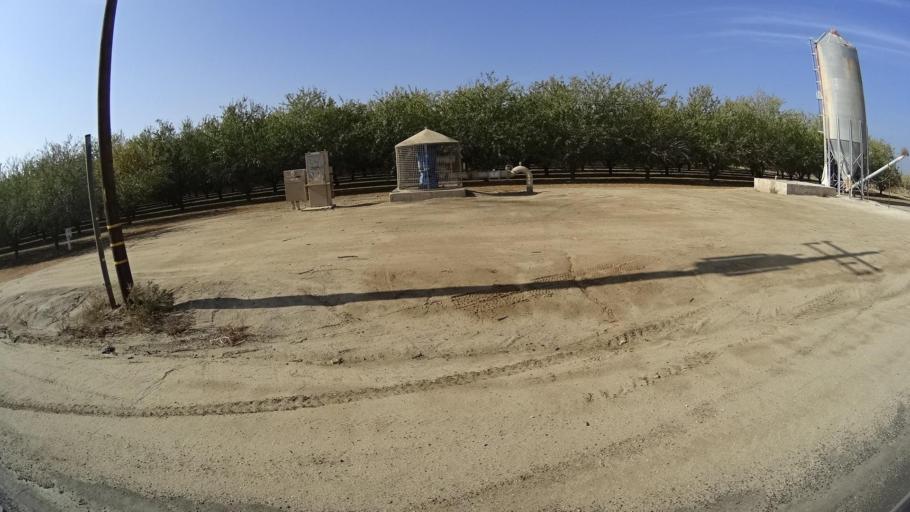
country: US
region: California
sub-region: Kern County
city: Shafter
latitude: 35.5365
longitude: -119.1514
